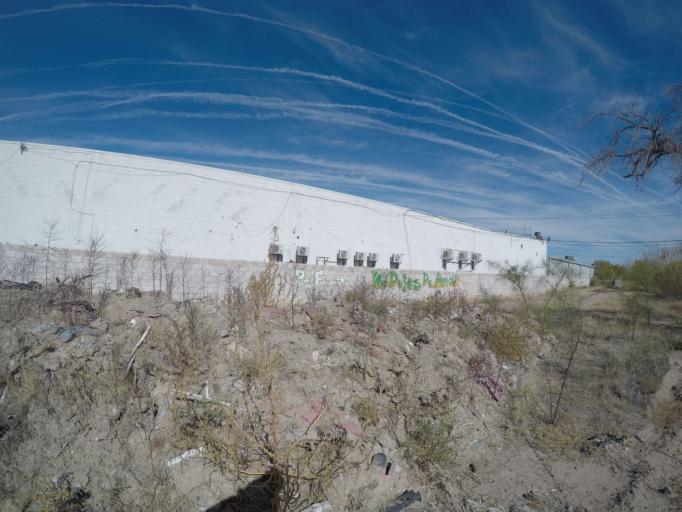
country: MX
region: Chihuahua
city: Ciudad Juarez
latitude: 31.7347
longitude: -106.4437
